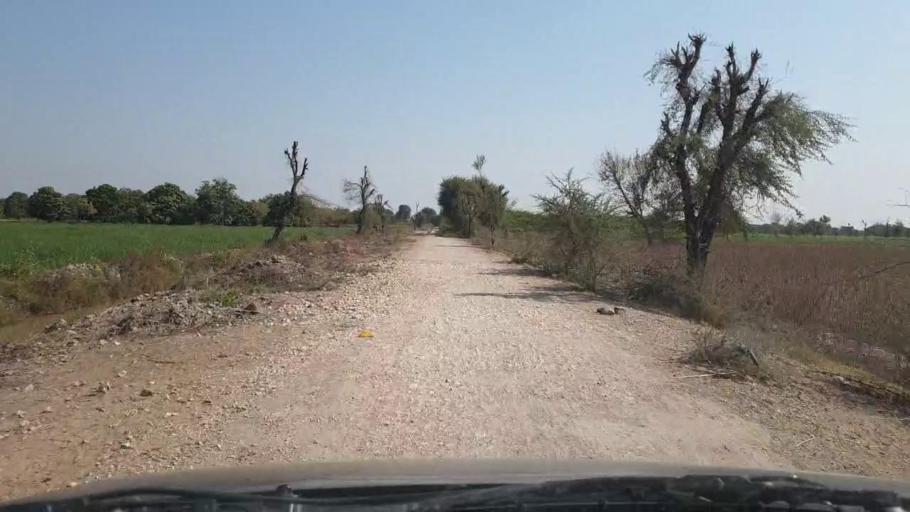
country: PK
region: Sindh
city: Digri
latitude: 25.2023
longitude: 69.2360
